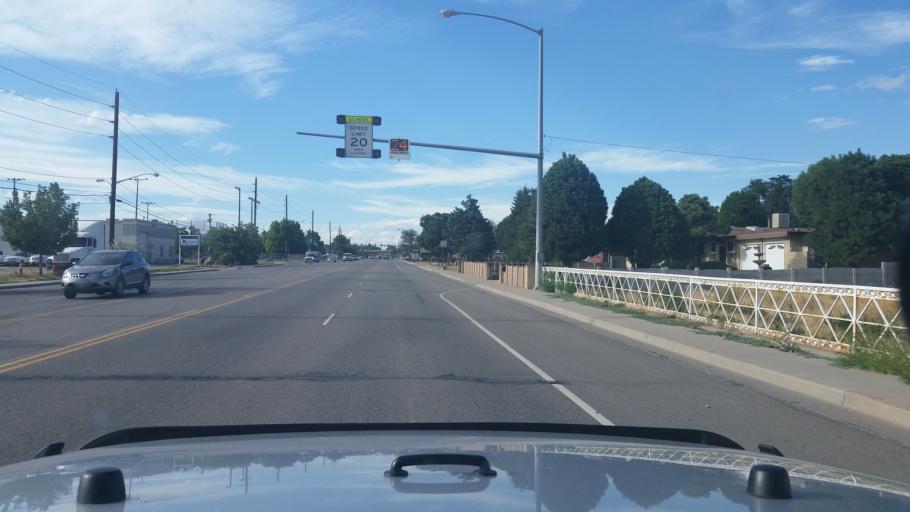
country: US
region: Colorado
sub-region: Adams County
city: Twin Lakes
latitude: 39.8206
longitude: -105.0062
